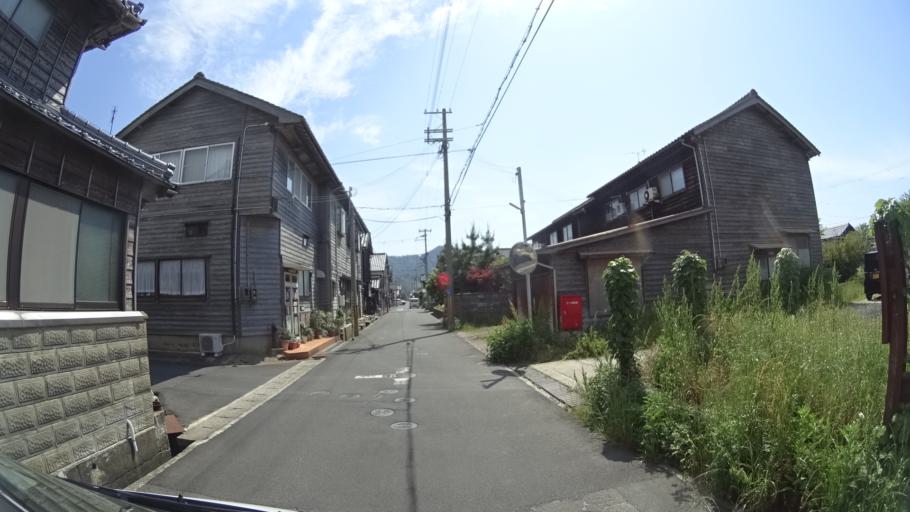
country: JP
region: Kyoto
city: Miyazu
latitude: 35.6869
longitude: 135.0280
